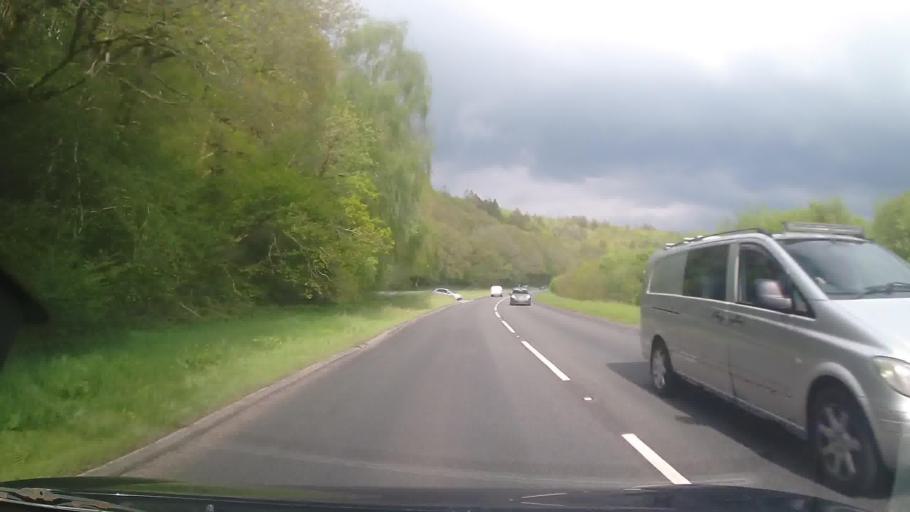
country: GB
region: Wales
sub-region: Gwynedd
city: Penrhyndeudraeth
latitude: 52.9419
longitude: -4.0368
